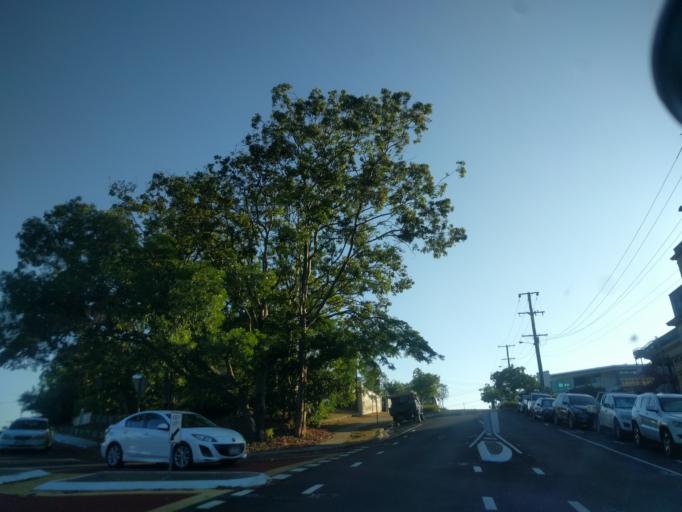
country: AU
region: Queensland
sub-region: Brisbane
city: Fortitude Valley
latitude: -27.4482
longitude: 153.0231
